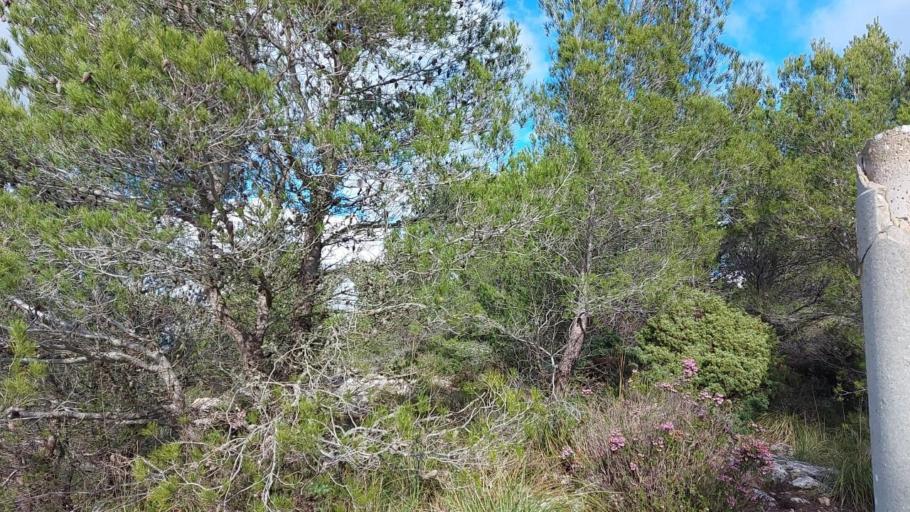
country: ES
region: Balearic Islands
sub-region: Illes Balears
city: Alaro
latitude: 39.7373
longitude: 2.8140
